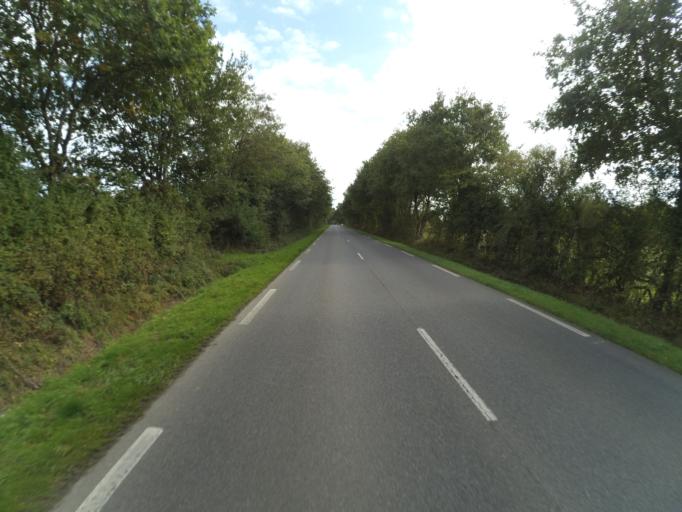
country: FR
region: Pays de la Loire
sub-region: Departement de la Loire-Atlantique
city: Plesse
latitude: 47.5073
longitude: -1.8756
